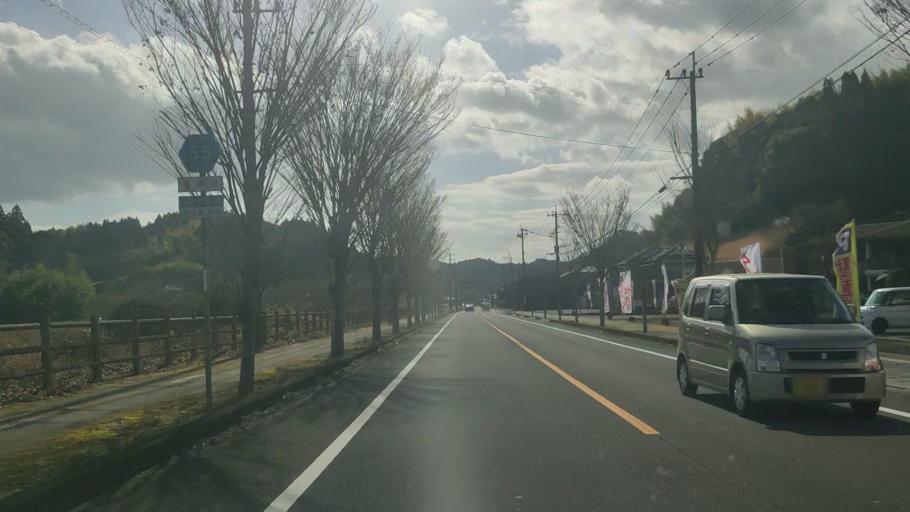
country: JP
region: Kagoshima
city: Okuchi-shinohara
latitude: 31.9466
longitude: 130.7113
